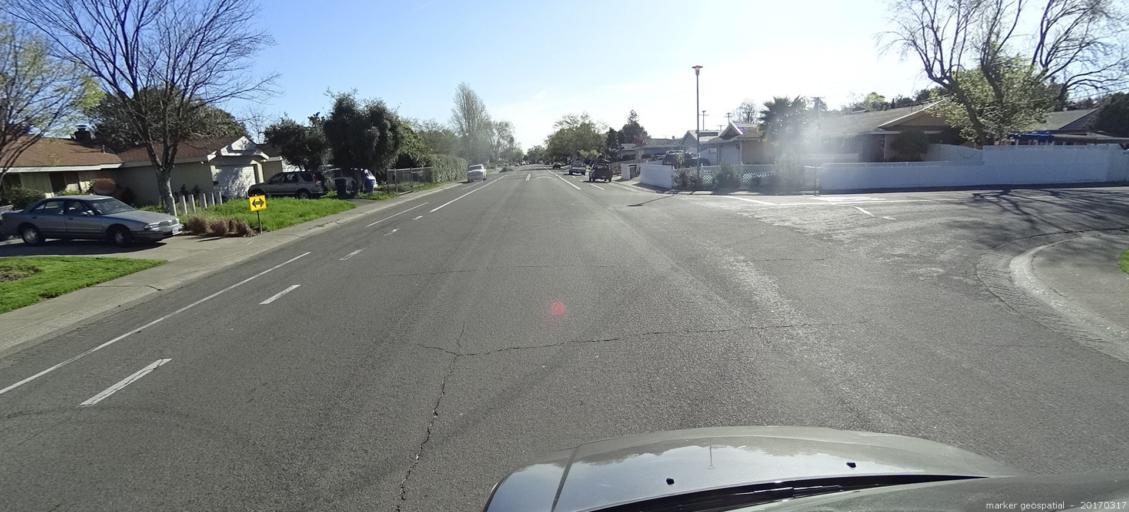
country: US
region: California
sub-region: Sacramento County
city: Parkway
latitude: 38.4890
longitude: -121.4972
